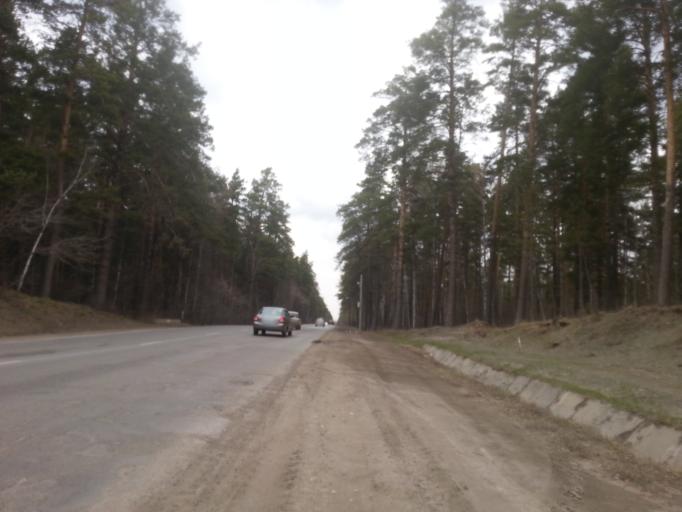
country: RU
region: Altai Krai
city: Yuzhnyy
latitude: 53.2715
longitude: 83.7240
